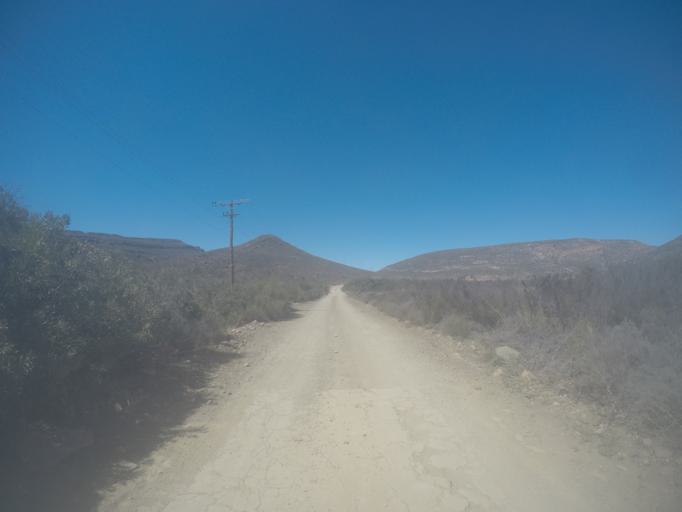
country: ZA
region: Western Cape
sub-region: West Coast District Municipality
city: Clanwilliam
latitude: -32.5189
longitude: 19.3505
